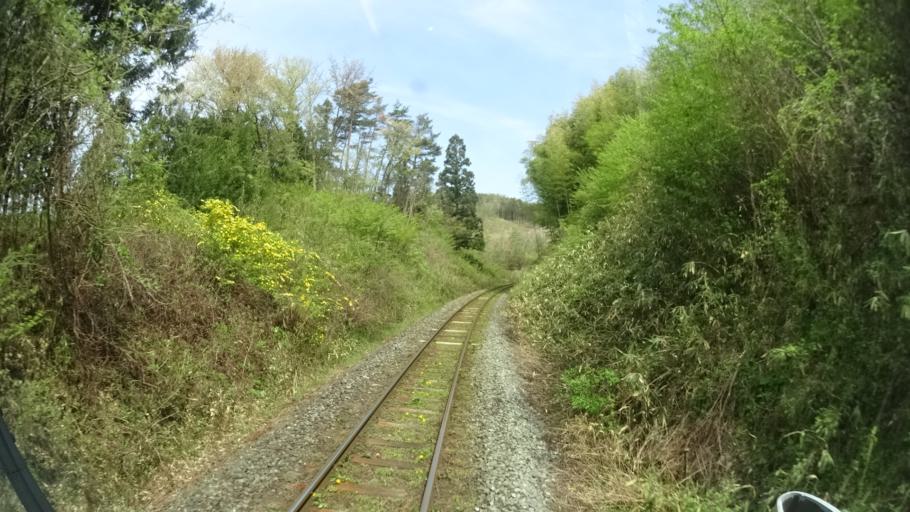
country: JP
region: Iwate
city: Ichinoseki
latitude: 38.9991
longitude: 141.2600
